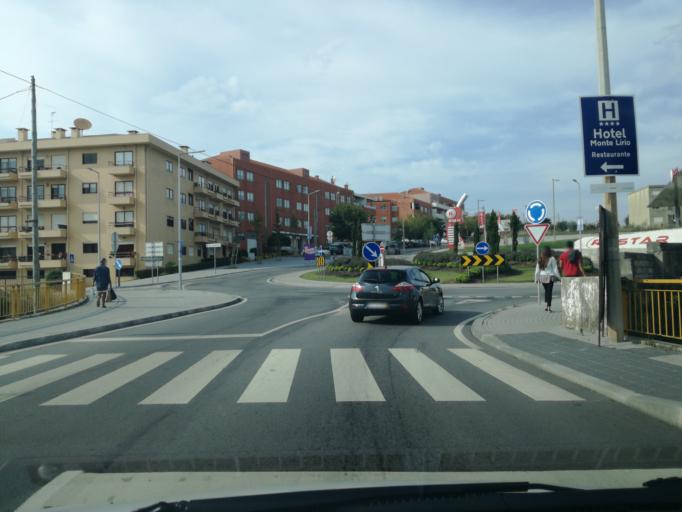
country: PT
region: Aveiro
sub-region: Espinho
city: Espinho
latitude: 41.0140
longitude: -8.6335
